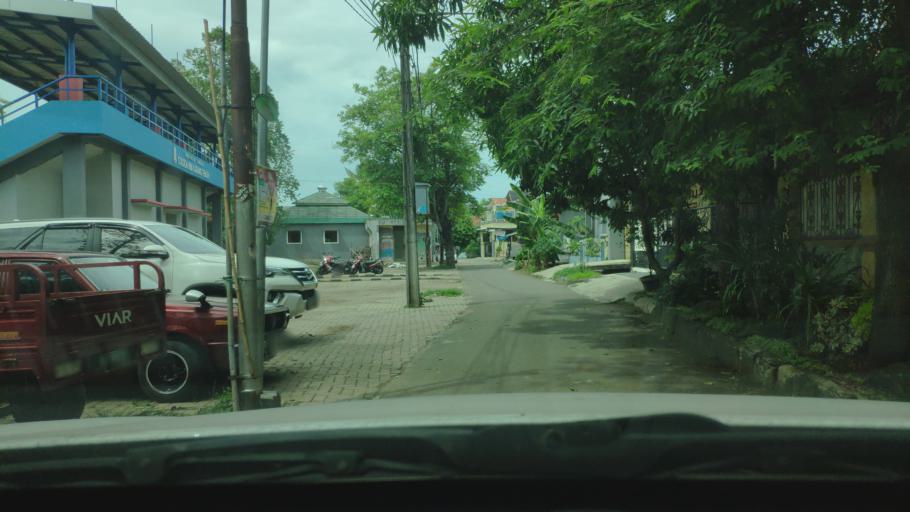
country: ID
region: West Java
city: Ciputat
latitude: -6.2241
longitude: 106.7041
